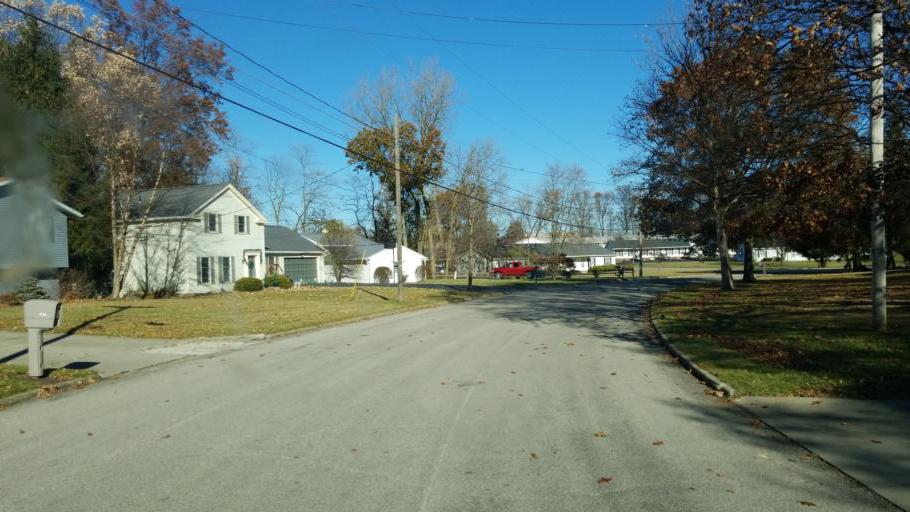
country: US
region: Ohio
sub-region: Ashland County
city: Ashland
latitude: 40.8485
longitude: -82.3388
